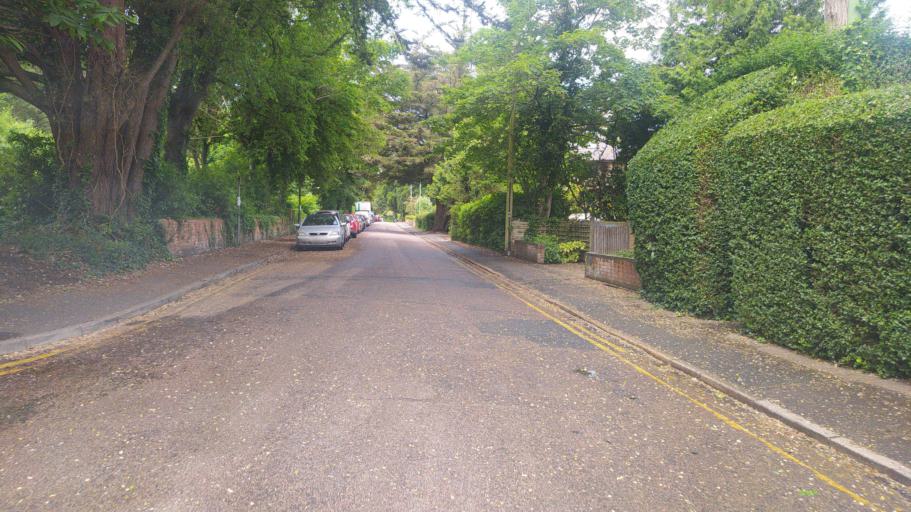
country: GB
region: England
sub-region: Bournemouth
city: Bournemouth
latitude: 50.7231
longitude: -1.8884
